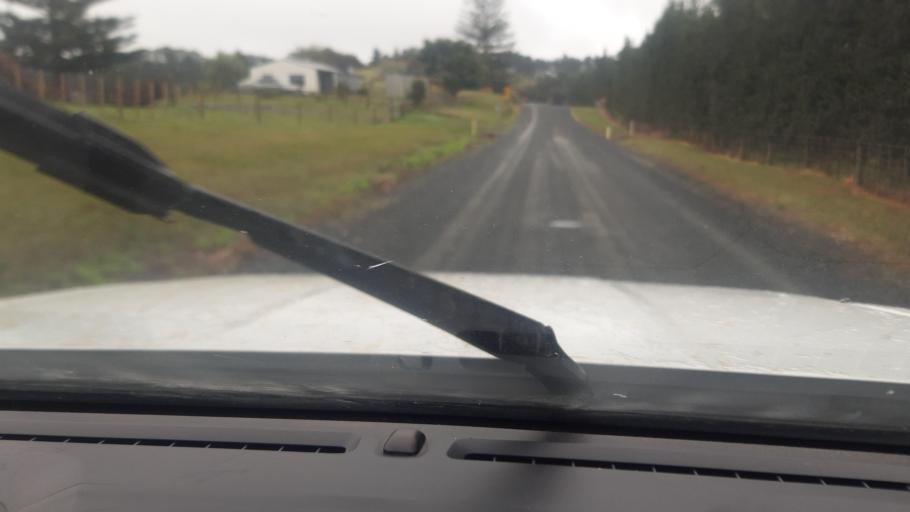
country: NZ
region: Northland
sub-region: Far North District
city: Kaitaia
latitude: -34.9762
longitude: 173.2038
